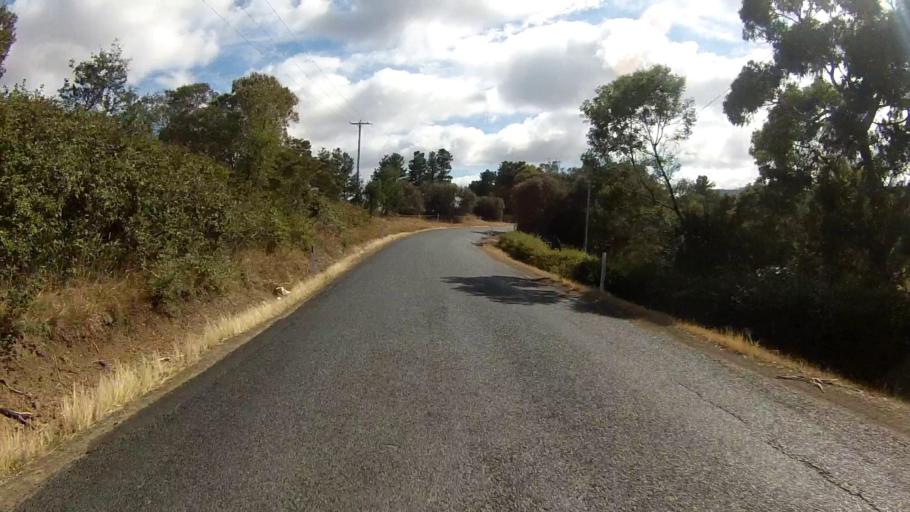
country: AU
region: Tasmania
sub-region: Brighton
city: Old Beach
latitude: -42.7732
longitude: 147.2880
